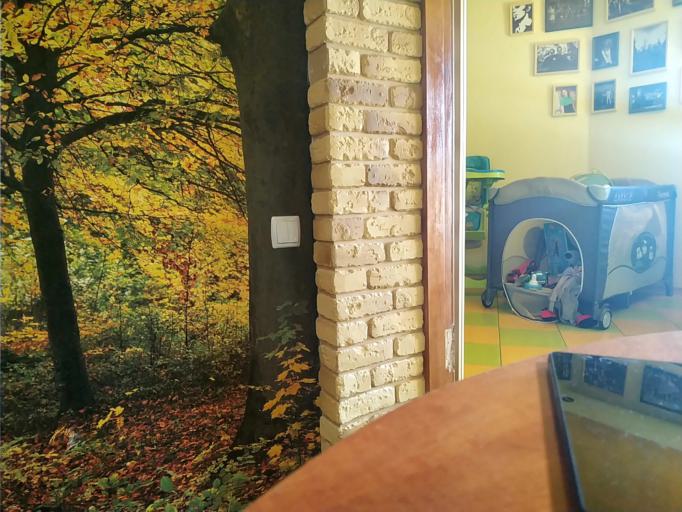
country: RU
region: Tverskaya
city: Krasnomayskiy
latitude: 57.6254
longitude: 34.4499
